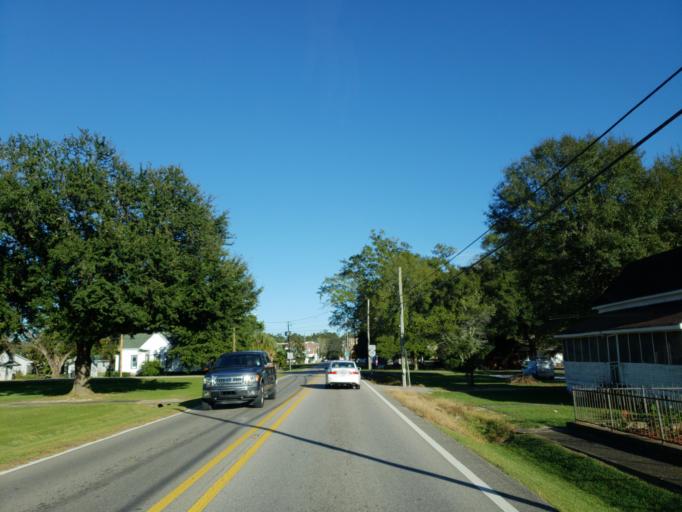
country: US
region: Mississippi
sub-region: Perry County
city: Richton
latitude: 31.3491
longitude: -88.9386
